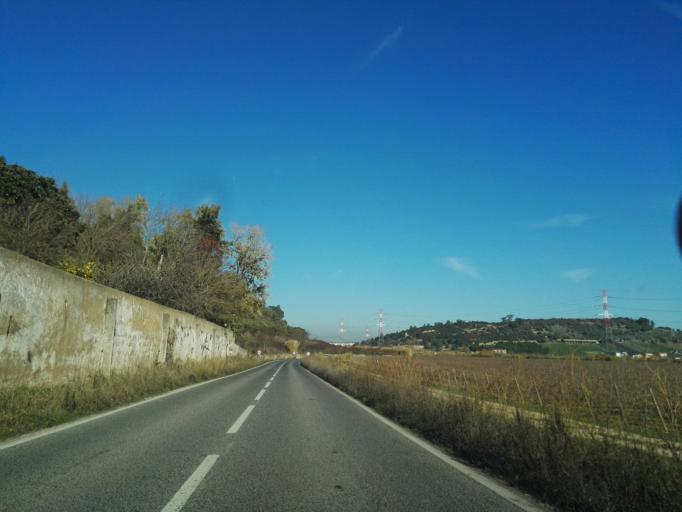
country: PT
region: Lisbon
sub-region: Alenquer
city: Carregado
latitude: 39.0076
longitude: -8.9884
